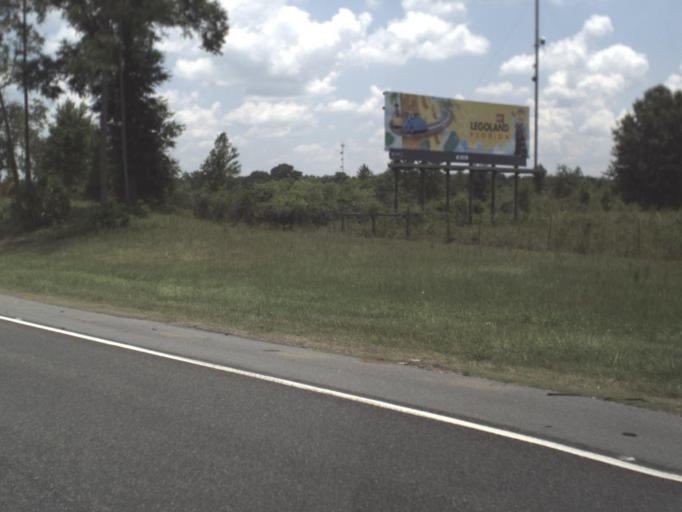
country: US
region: Florida
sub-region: Hamilton County
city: Jasper
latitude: 30.5152
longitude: -83.0546
